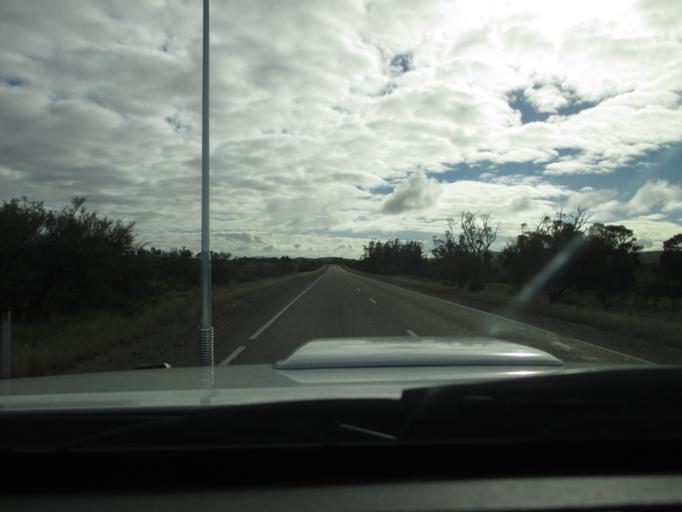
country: AU
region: South Australia
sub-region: Flinders Ranges
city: Quorn
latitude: -32.5047
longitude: 138.5472
